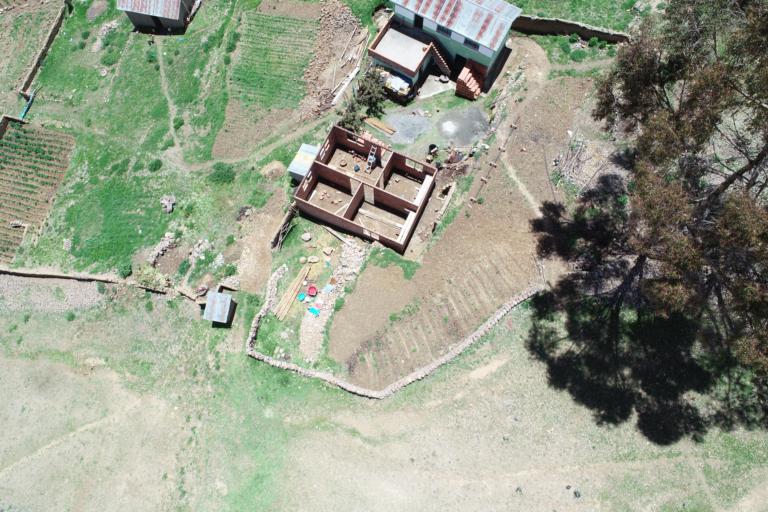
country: BO
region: La Paz
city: Achacachi
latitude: -16.0255
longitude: -68.7902
